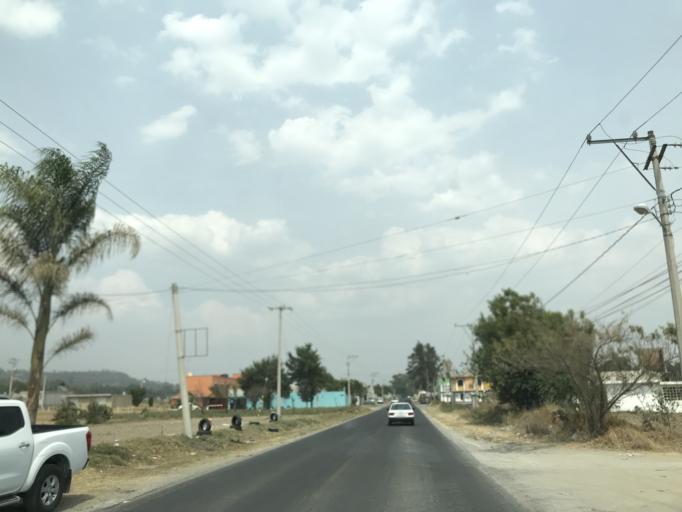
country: MX
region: Tlaxcala
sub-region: Panotla
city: Fraccionamiento la Virgen
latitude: 19.3202
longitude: -98.2839
